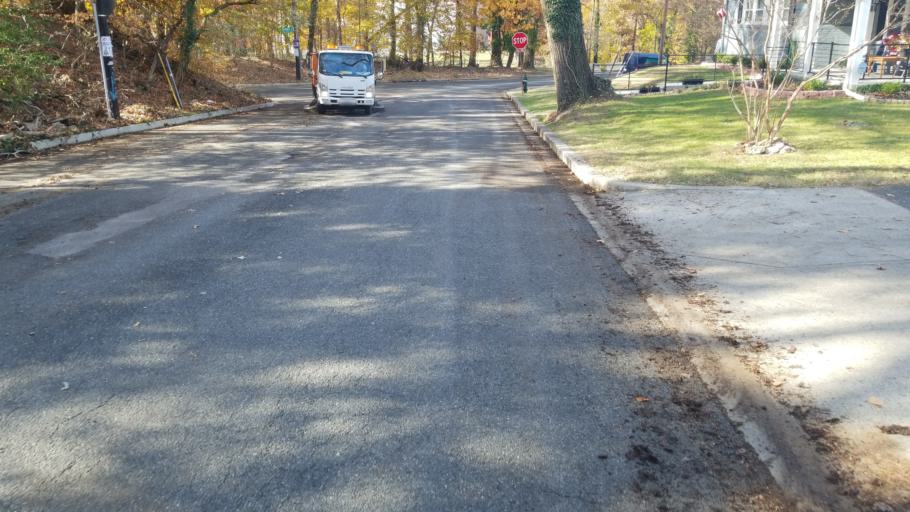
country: US
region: Maryland
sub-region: Prince George's County
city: Coral Hills
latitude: 38.8765
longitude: -76.9390
